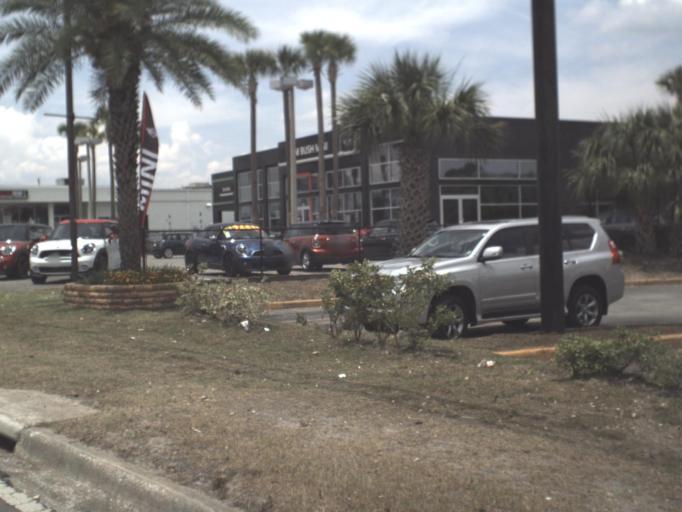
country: US
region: Florida
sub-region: Duval County
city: Jacksonville
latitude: 30.3227
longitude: -81.5416
